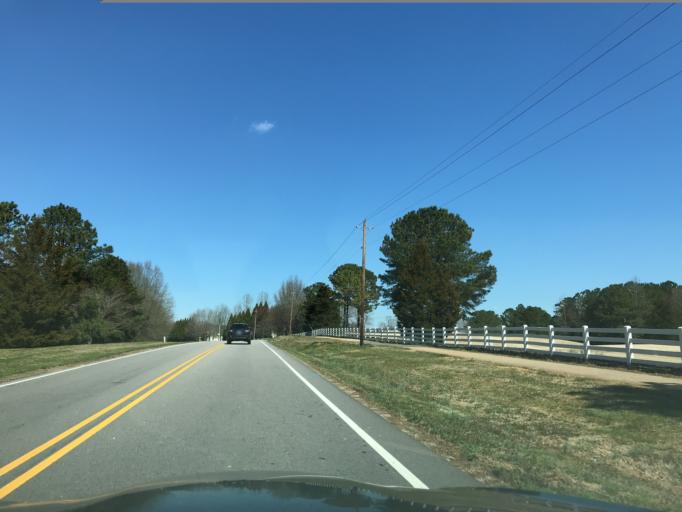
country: US
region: North Carolina
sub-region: Wake County
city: Wake Forest
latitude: 35.9590
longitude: -78.5642
